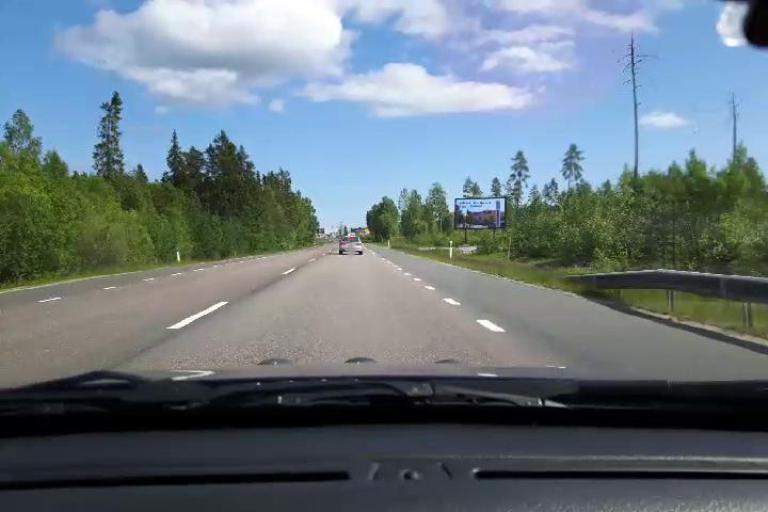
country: SE
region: Gaevleborg
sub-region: Hudiksvalls Kommun
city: Sorforsa
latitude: 61.7169
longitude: 17.0324
